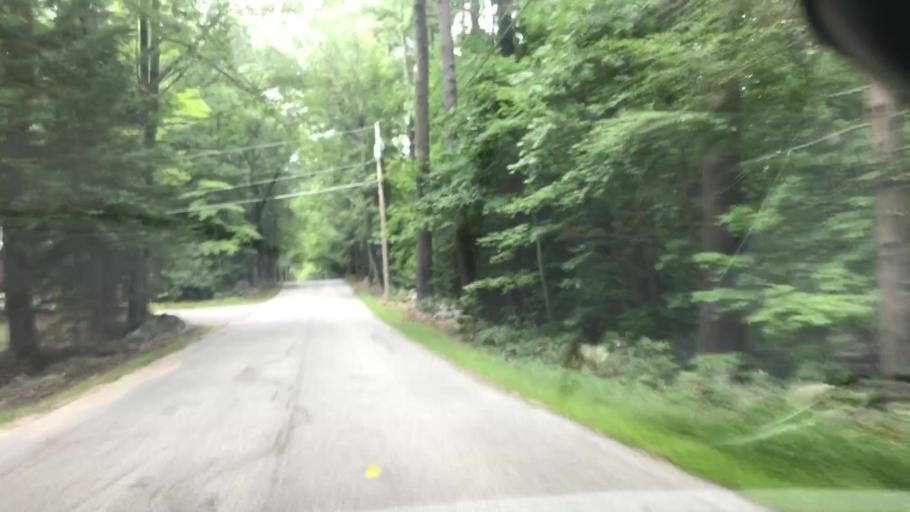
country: US
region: New Hampshire
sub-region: Hillsborough County
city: Milford
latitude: 42.8535
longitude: -71.6330
